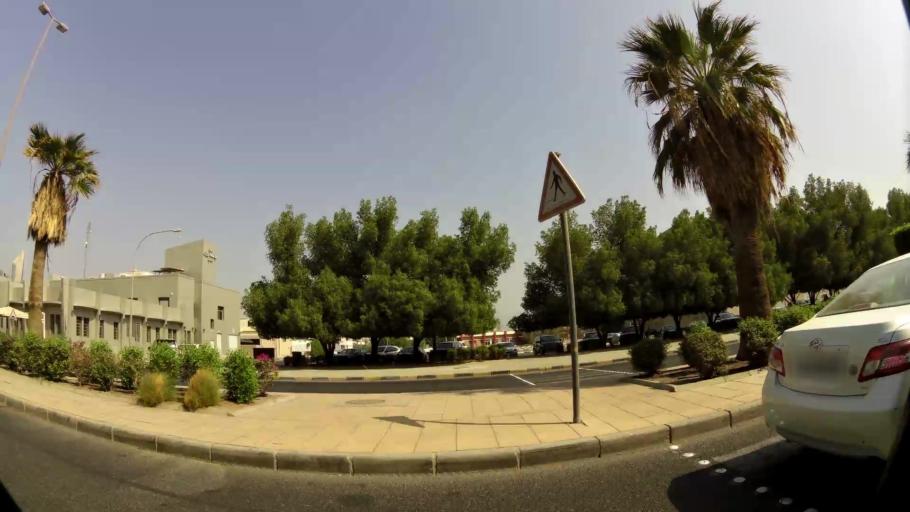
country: KW
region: Al Asimah
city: Ad Dasmah
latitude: 29.3583
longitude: 47.9969
